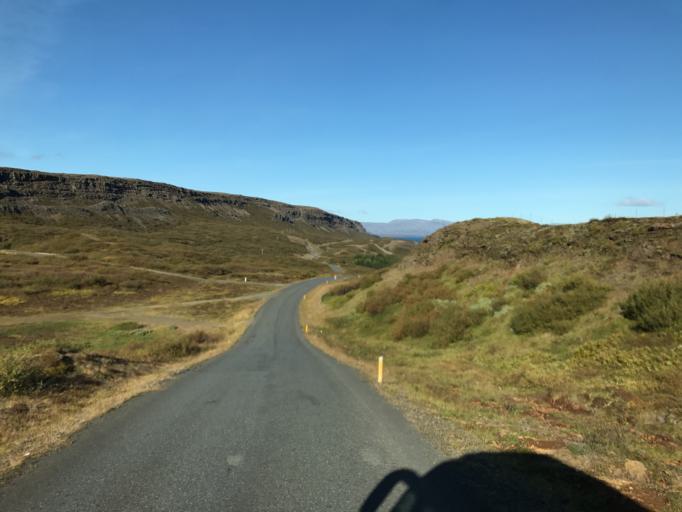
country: IS
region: South
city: Hveragerdi
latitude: 64.1474
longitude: -21.2587
